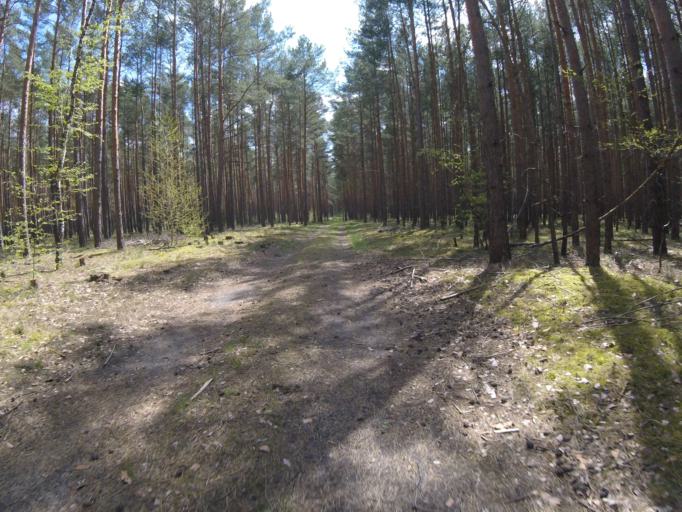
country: DE
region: Brandenburg
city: Gross Koris
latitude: 52.1878
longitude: 13.6853
